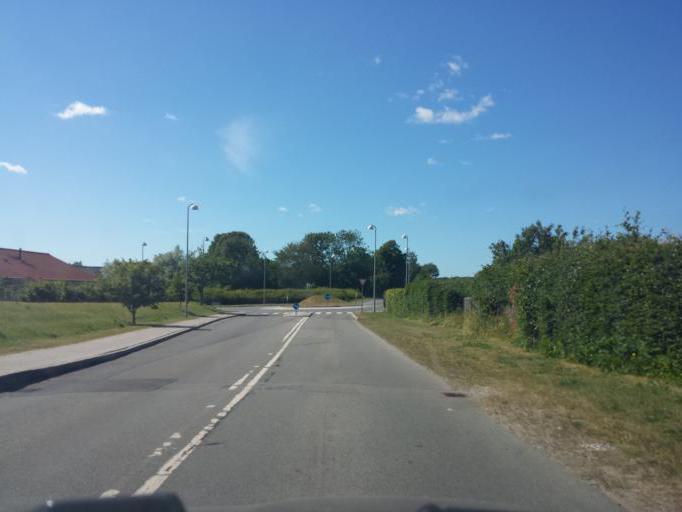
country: DK
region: Capital Region
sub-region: Egedal Kommune
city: Ganlose
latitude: 55.7964
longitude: 12.2588
